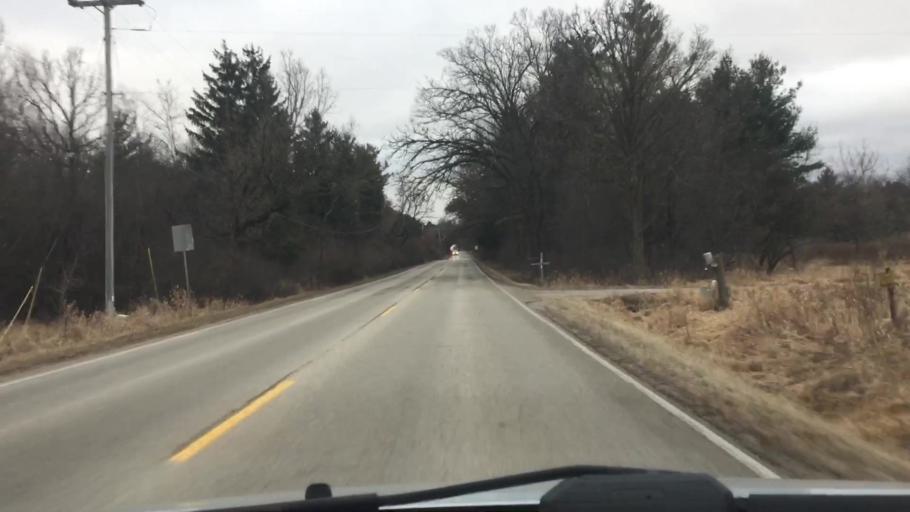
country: US
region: Wisconsin
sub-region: Waukesha County
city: Delafield
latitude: 43.0380
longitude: -88.4043
